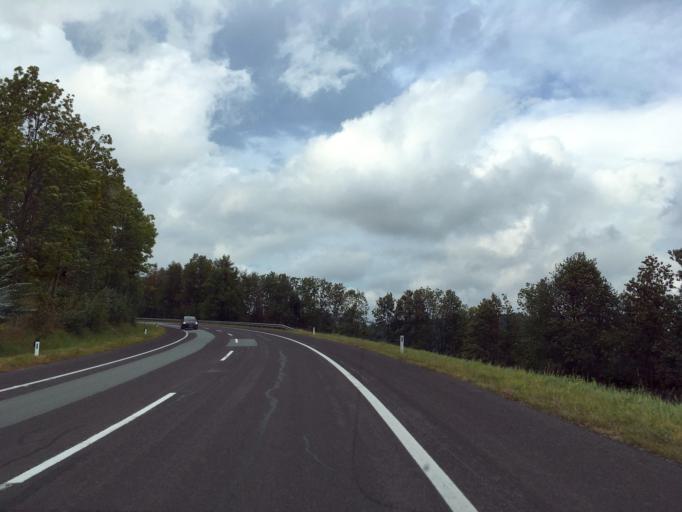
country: AT
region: Lower Austria
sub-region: Politischer Bezirk Neunkirchen
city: Monichkirchen
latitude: 47.4900
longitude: 16.0416
